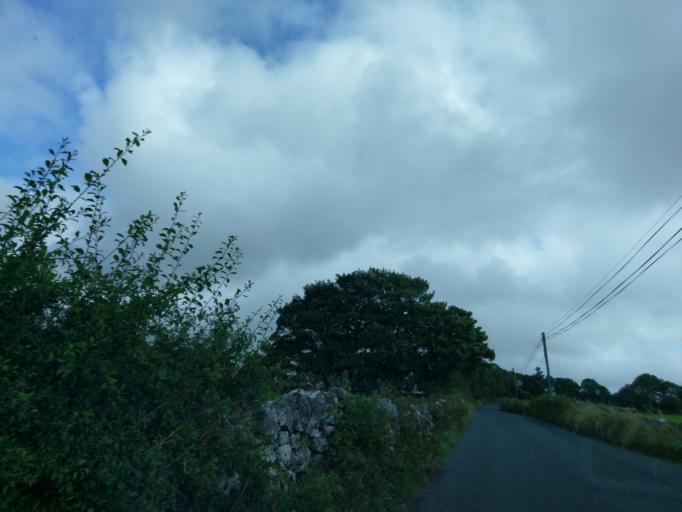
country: IE
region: Connaught
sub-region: County Galway
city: Athenry
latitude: 53.3237
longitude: -8.7835
